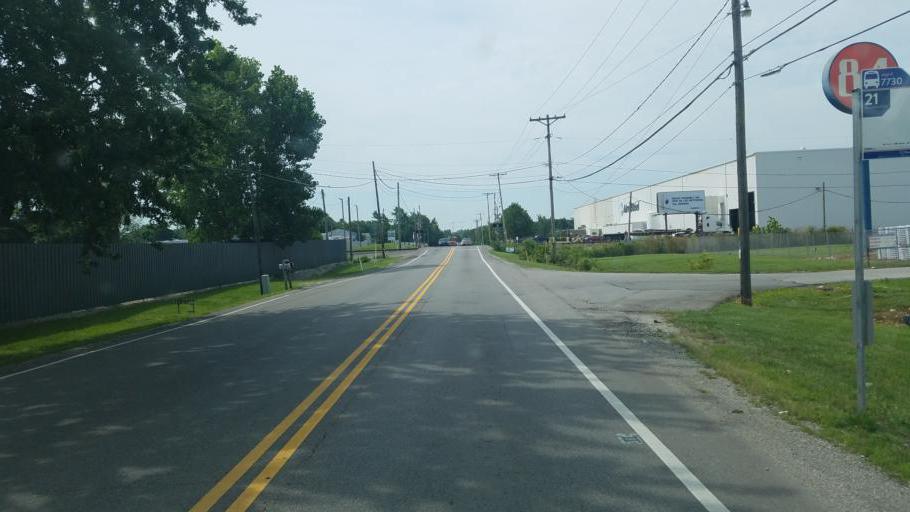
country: US
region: Ohio
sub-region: Franklin County
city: Lincoln Village
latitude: 39.9632
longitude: -83.1467
